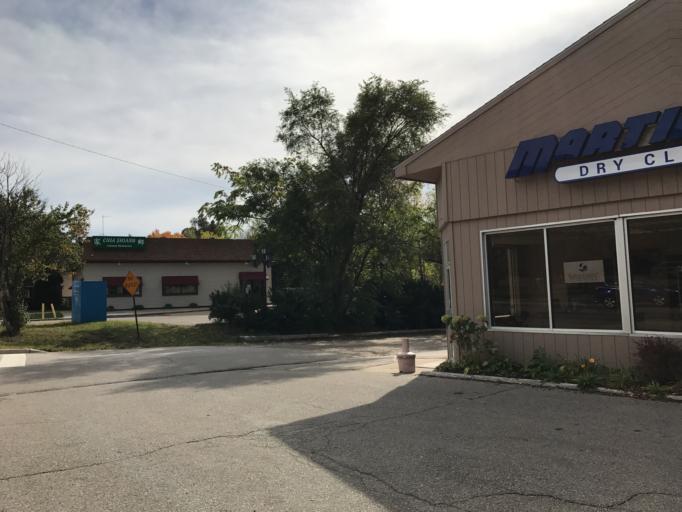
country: US
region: Michigan
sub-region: Washtenaw County
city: Ann Arbor
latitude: 42.2576
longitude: -83.7278
